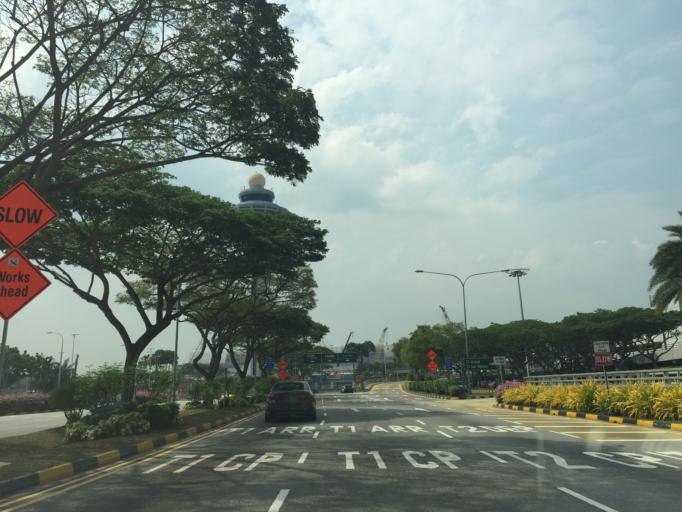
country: SG
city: Singapore
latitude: 1.3573
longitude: 103.9888
